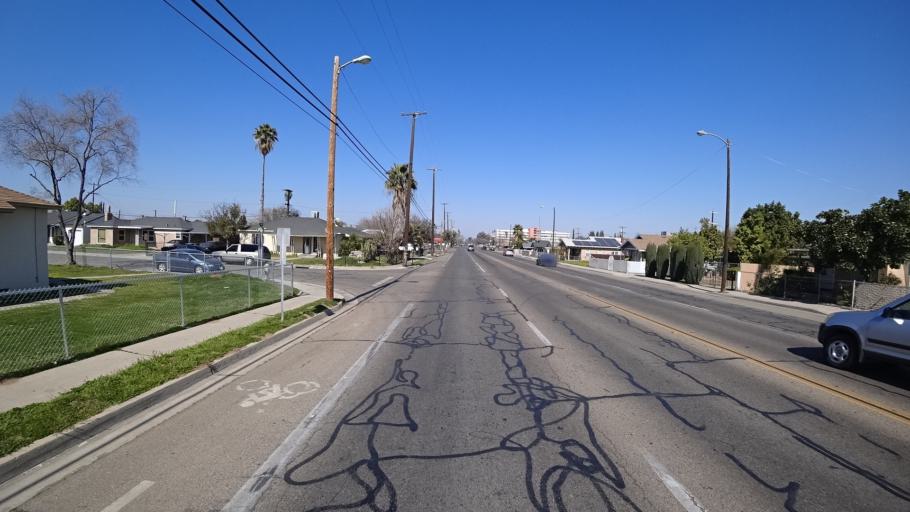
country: US
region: California
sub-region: Fresno County
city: Fresno
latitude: 36.7335
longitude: -119.7547
